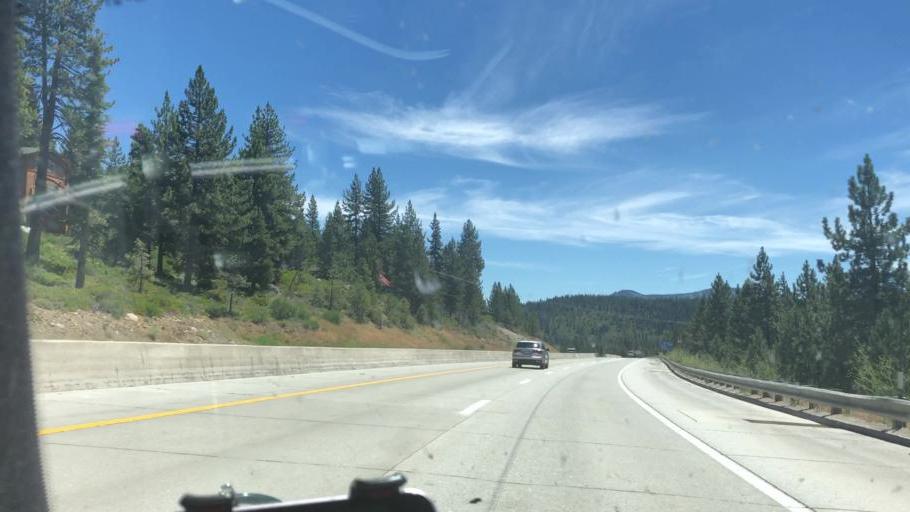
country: US
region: California
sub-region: Nevada County
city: Truckee
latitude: 39.3289
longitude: -120.2425
